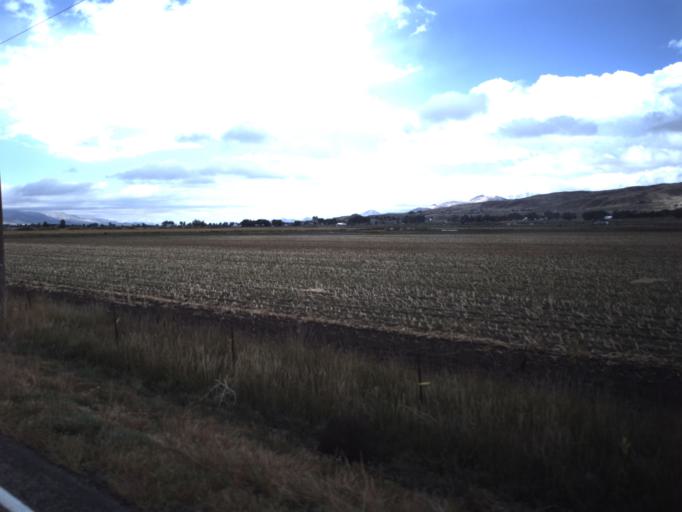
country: US
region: Utah
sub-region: Sevier County
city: Monroe
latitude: 38.6562
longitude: -112.1215
